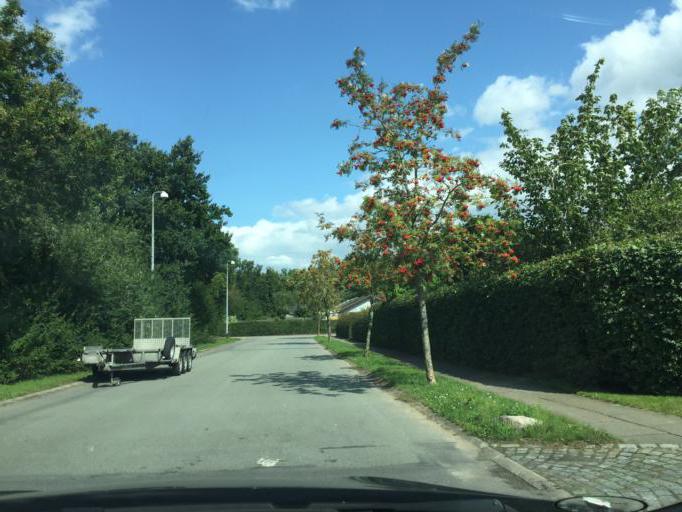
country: DK
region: South Denmark
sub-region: Odense Kommune
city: Neder Holluf
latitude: 55.3673
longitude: 10.4489
